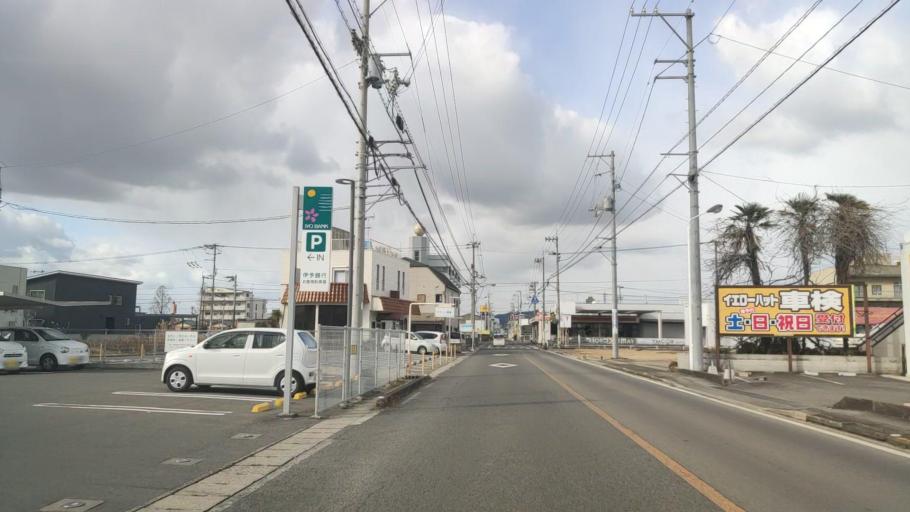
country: JP
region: Ehime
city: Saijo
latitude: 34.0507
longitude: 133.0136
